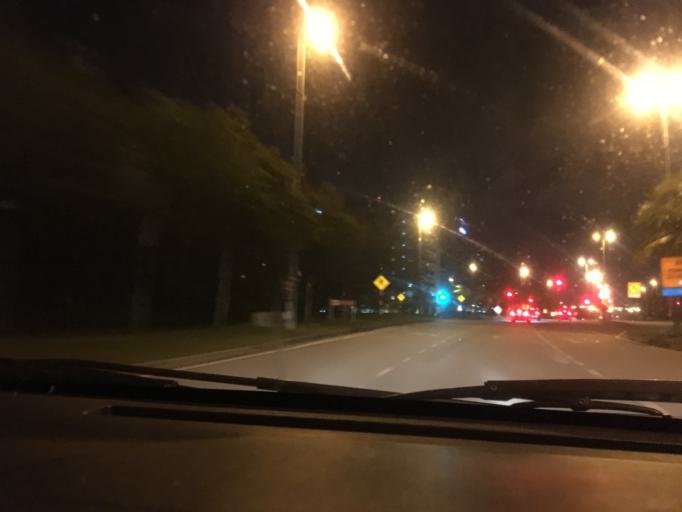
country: MY
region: Putrajaya
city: Putrajaya
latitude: 2.9112
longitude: 101.6498
